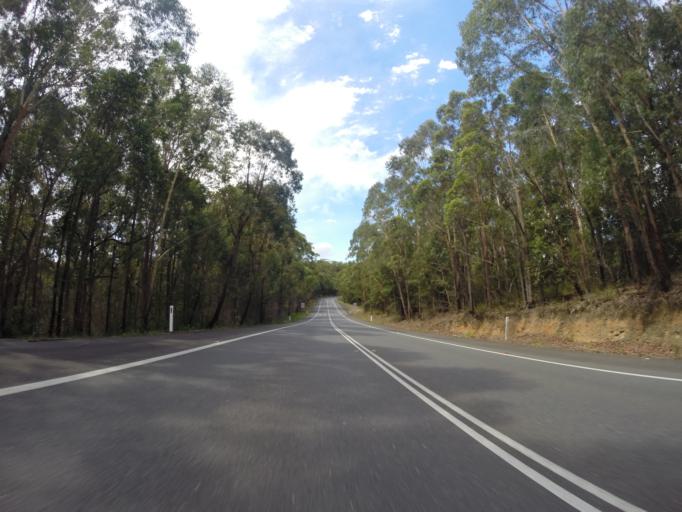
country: AU
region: New South Wales
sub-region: Shoalhaven Shire
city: Milton
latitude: -35.1552
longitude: 150.4505
